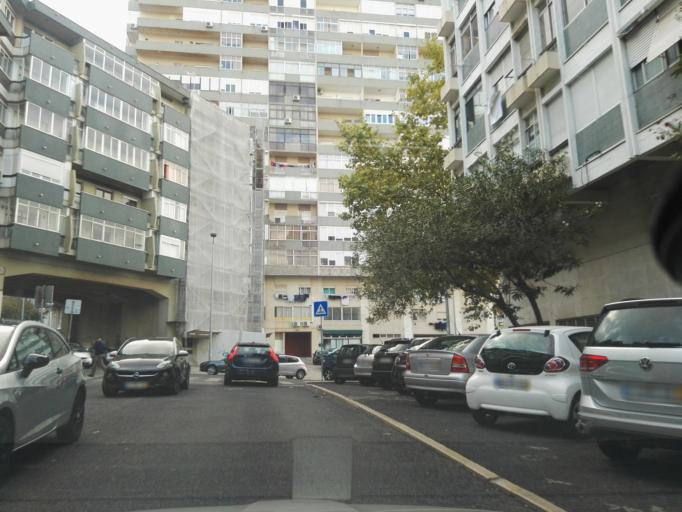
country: PT
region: Lisbon
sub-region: Lisbon
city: Lisbon
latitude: 38.7385
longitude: -9.1222
